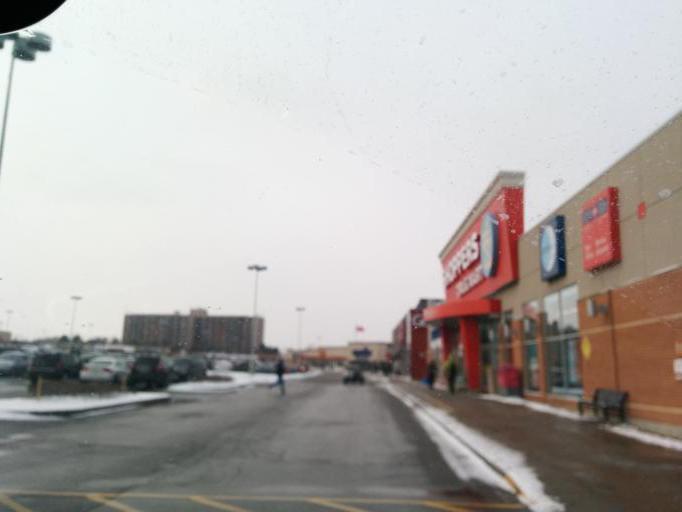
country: CA
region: Ontario
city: Mississauga
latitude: 43.5819
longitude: -79.7583
